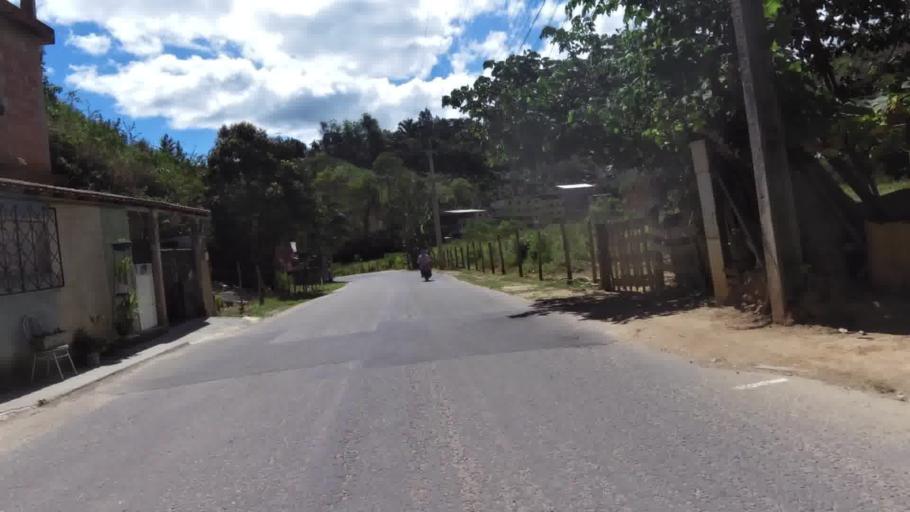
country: BR
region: Espirito Santo
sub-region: Vargem Alta
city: Vargem Alta
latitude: -20.6724
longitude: -41.0038
